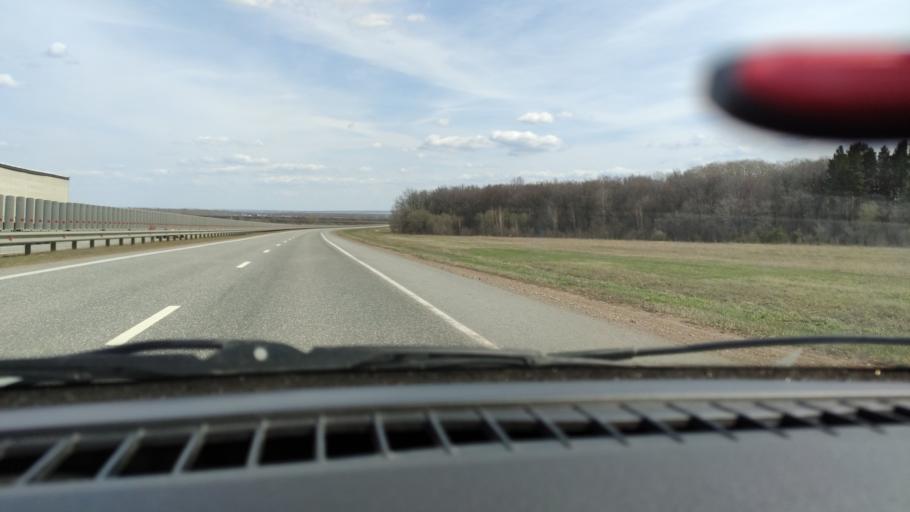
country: RU
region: Bashkortostan
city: Kushnarenkovo
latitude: 55.0673
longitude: 55.3461
